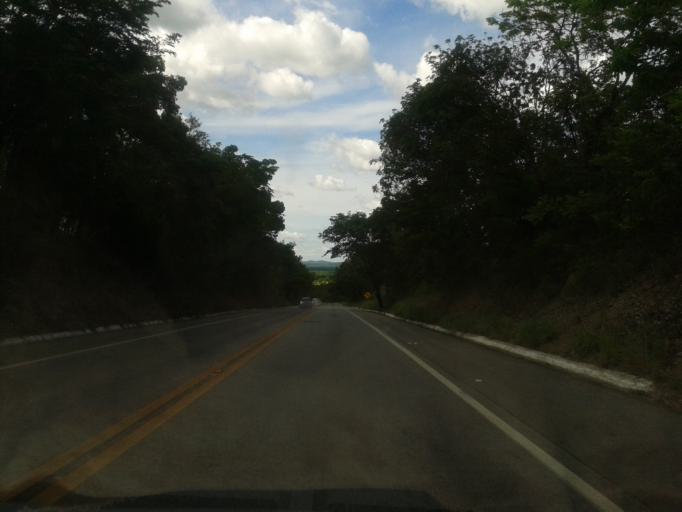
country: BR
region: Goias
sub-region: Itapuranga
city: Itapuranga
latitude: -15.5467
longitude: -50.2884
